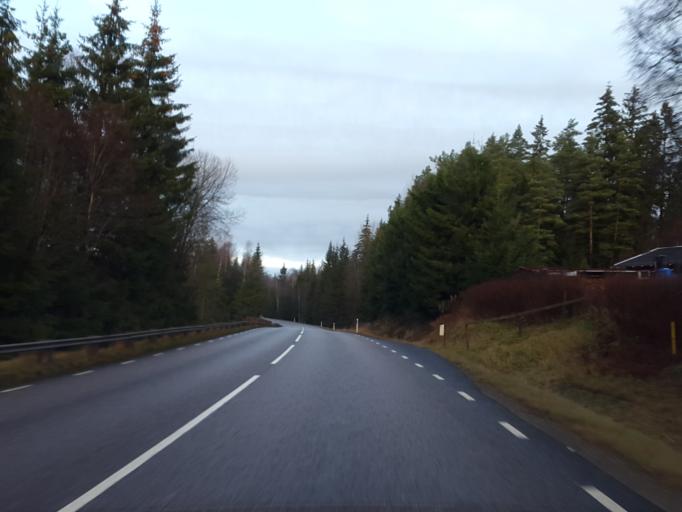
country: SE
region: Vaestra Goetaland
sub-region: Boras Kommun
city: Sandared
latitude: 57.7840
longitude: 12.7801
